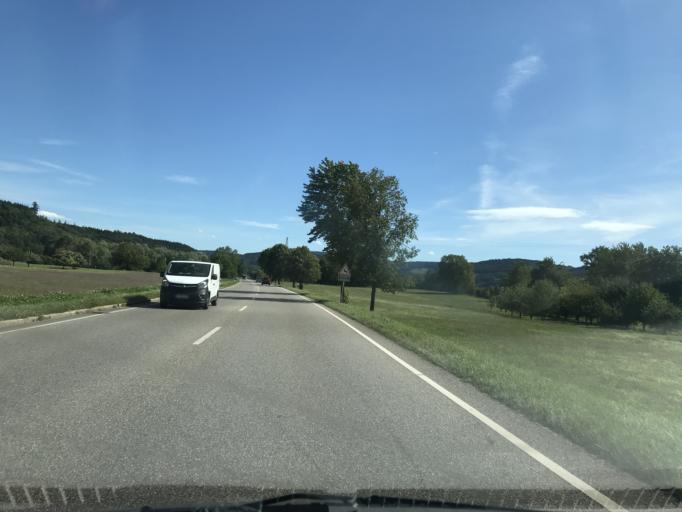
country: CH
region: Aargau
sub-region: Bezirk Rheinfelden
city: Mumpf
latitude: 47.5779
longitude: 7.9121
